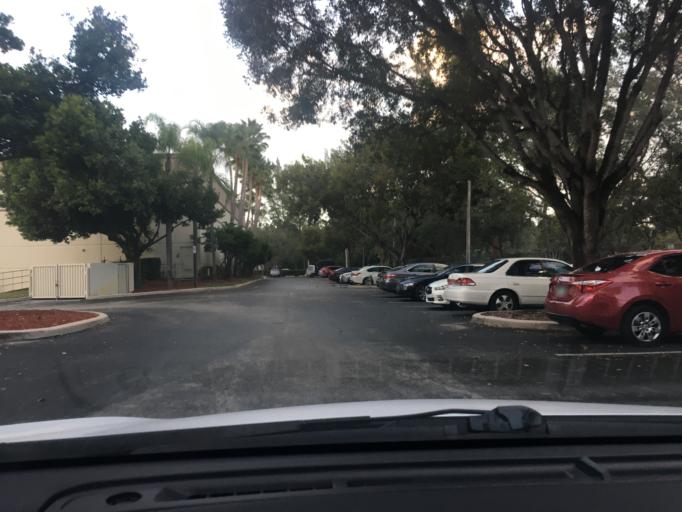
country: US
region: Florida
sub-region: Broward County
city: Dania Beach
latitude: 26.0705
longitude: -80.1788
